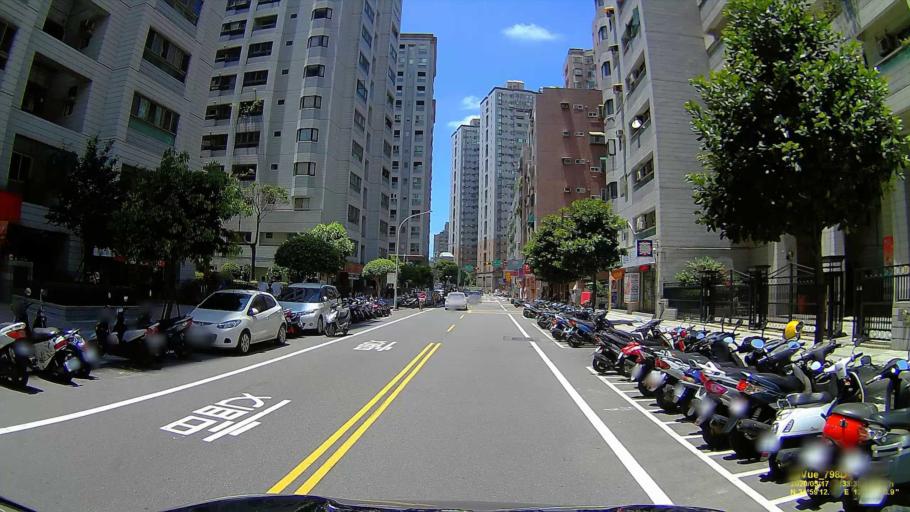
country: TW
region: Taiwan
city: Taoyuan City
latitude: 24.9868
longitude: 121.2885
